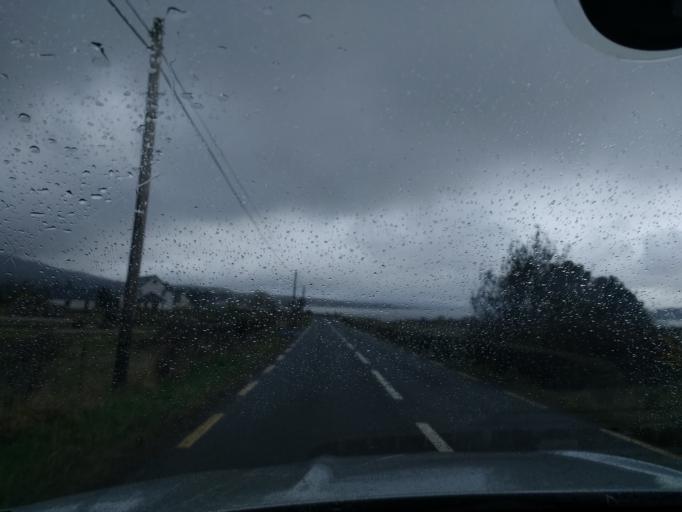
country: IE
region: Ulster
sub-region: County Donegal
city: Ramelton
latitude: 55.0671
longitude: -7.6025
